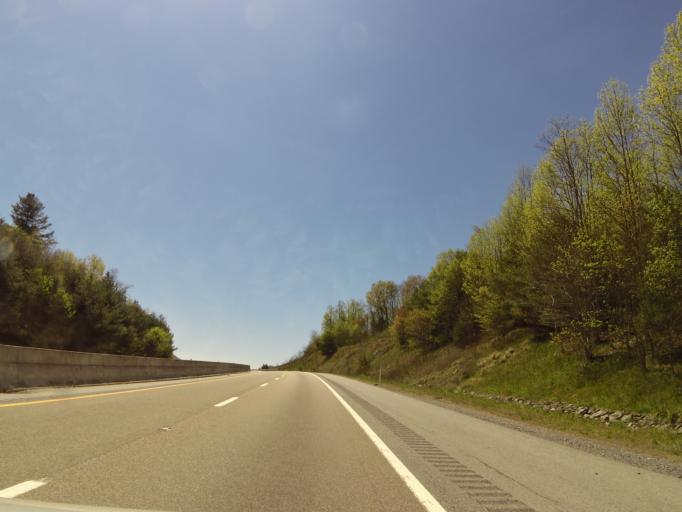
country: US
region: Tennessee
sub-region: Unicoi County
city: Banner Hill
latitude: 36.0447
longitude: -82.5243
